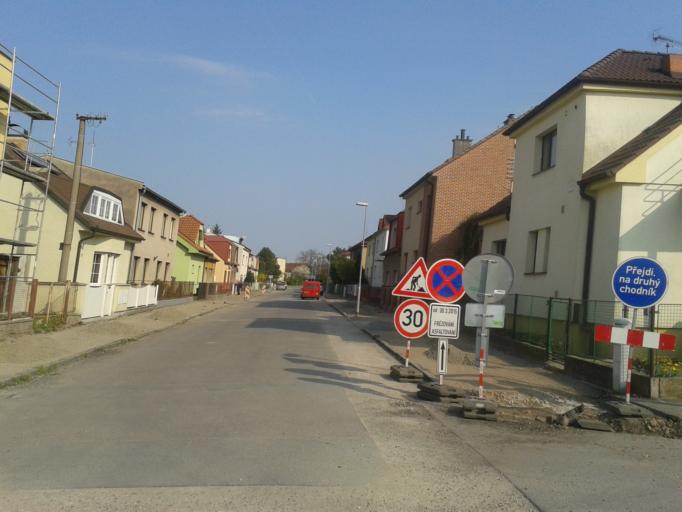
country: CZ
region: Pardubicky
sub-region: Okres Pardubice
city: Pardubice
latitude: 50.0358
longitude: 15.8013
